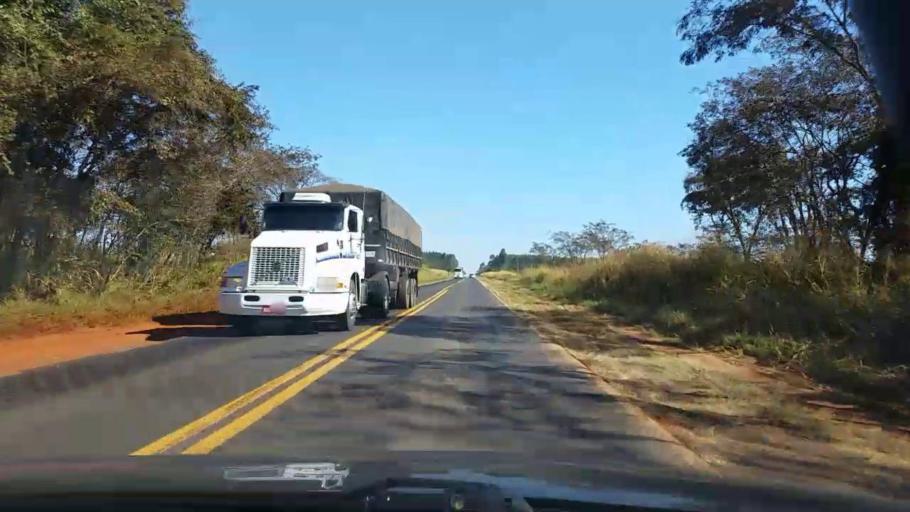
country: BR
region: Sao Paulo
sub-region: Avare
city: Avare
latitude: -22.9155
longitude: -48.7786
